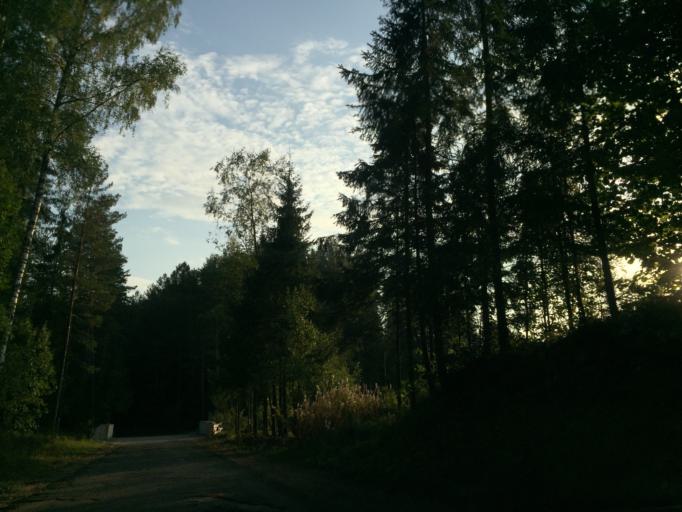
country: LV
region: Baldone
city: Baldone
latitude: 56.7735
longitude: 24.4004
